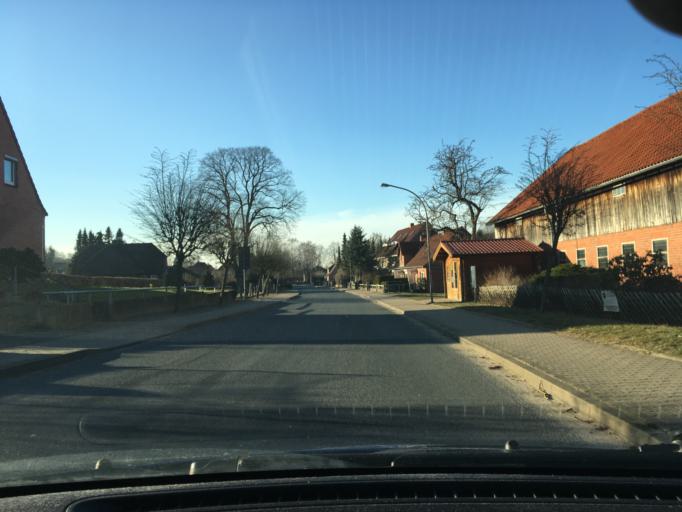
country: DE
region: Schleswig-Holstein
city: Mussen
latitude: 53.4945
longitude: 10.5622
